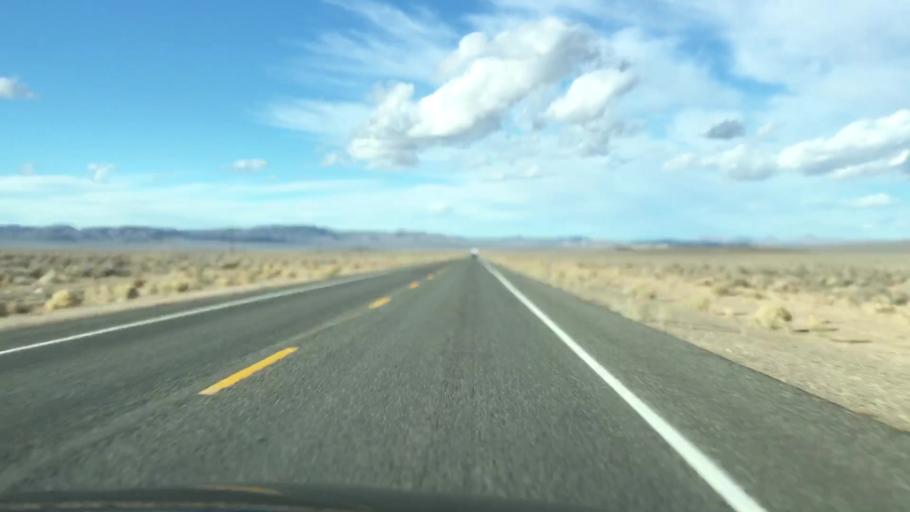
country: US
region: Nevada
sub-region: Esmeralda County
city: Goldfield
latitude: 37.4033
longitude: -117.1500
